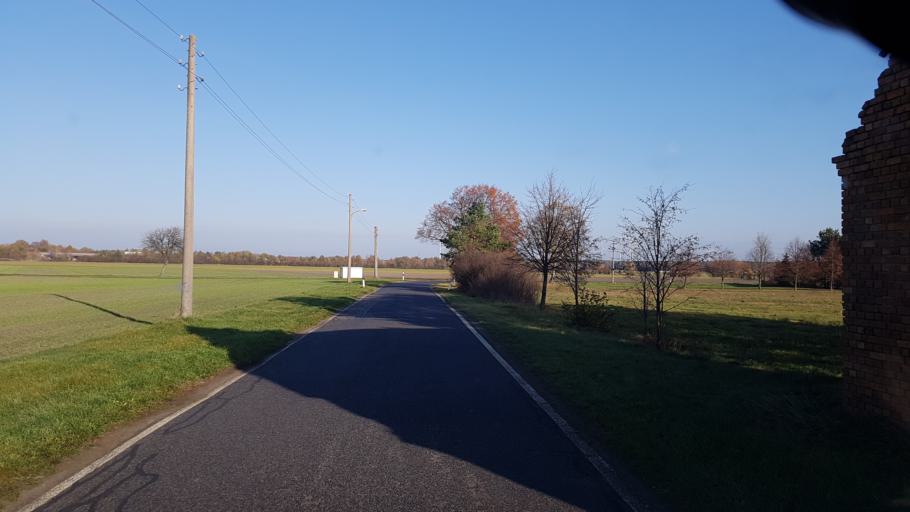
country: DE
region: Brandenburg
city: Grossraschen
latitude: 51.5808
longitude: 13.9418
